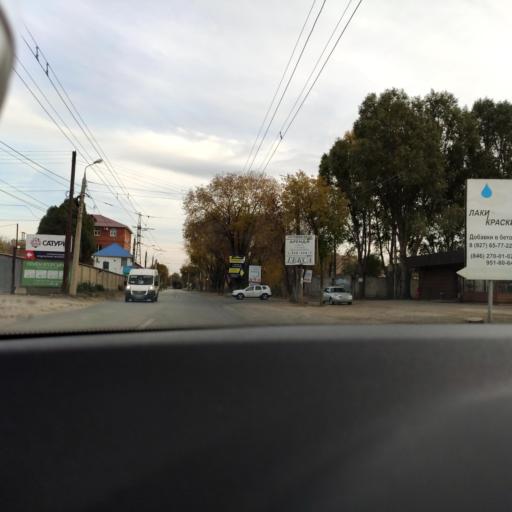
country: RU
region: Samara
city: Samara
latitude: 53.1940
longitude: 50.2736
